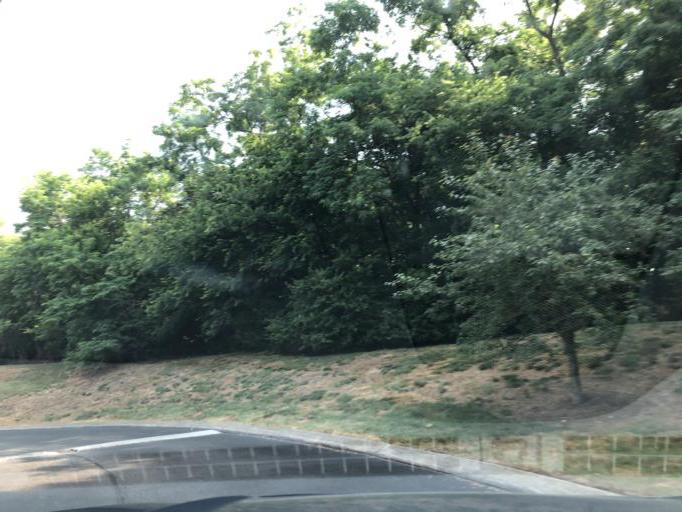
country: US
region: Tennessee
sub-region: Rutherford County
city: La Vergne
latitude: 36.0578
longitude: -86.6382
